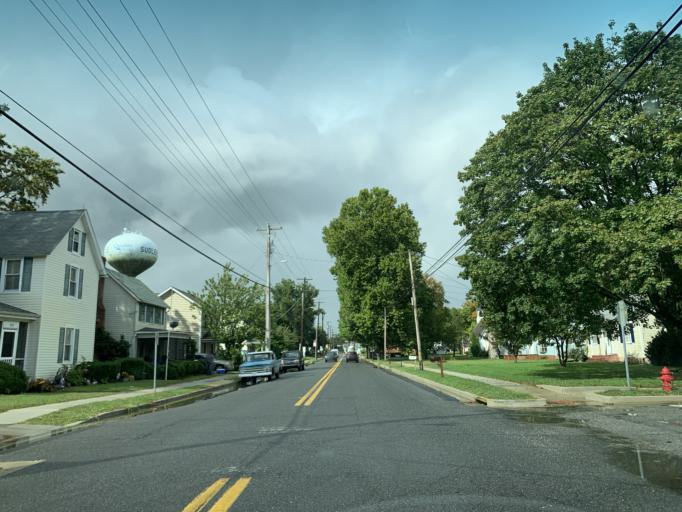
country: US
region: Maryland
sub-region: Queen Anne's County
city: Kingstown
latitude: 39.1839
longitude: -75.8582
